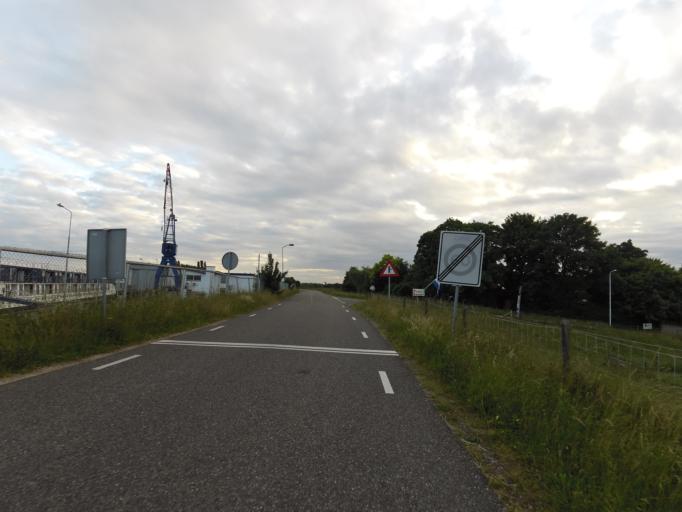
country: NL
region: Gelderland
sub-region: Gemeente Duiven
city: Duiven
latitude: 51.8792
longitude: 5.9947
